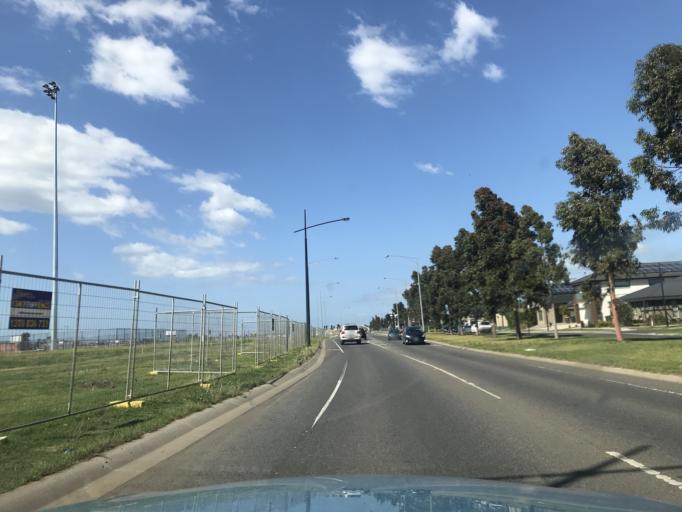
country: AU
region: Victoria
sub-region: Wyndham
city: Williams Landing
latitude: -37.8603
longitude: 144.7480
